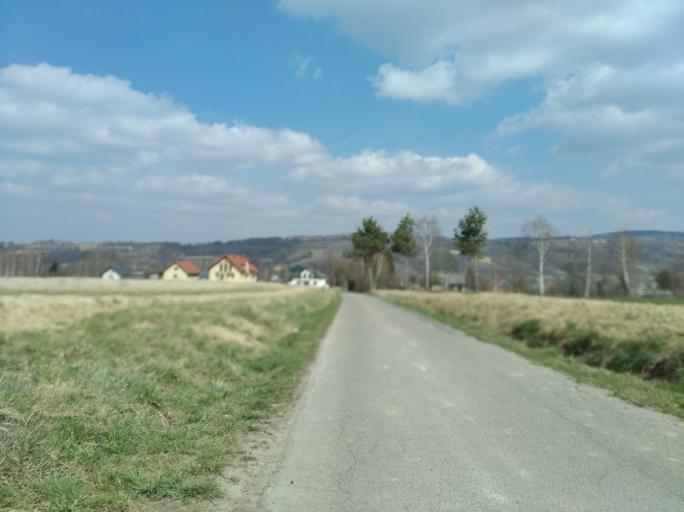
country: PL
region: Subcarpathian Voivodeship
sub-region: Powiat strzyzowski
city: Strzyzow
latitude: 49.8382
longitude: 21.8087
